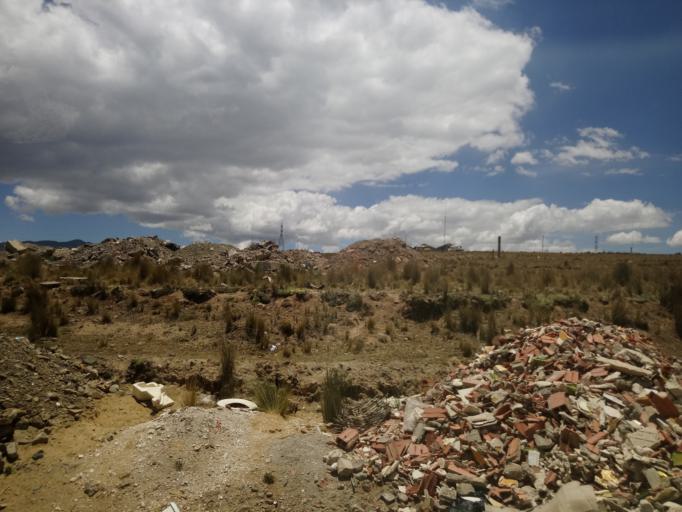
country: BO
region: La Paz
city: La Paz
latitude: -16.4405
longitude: -68.1635
